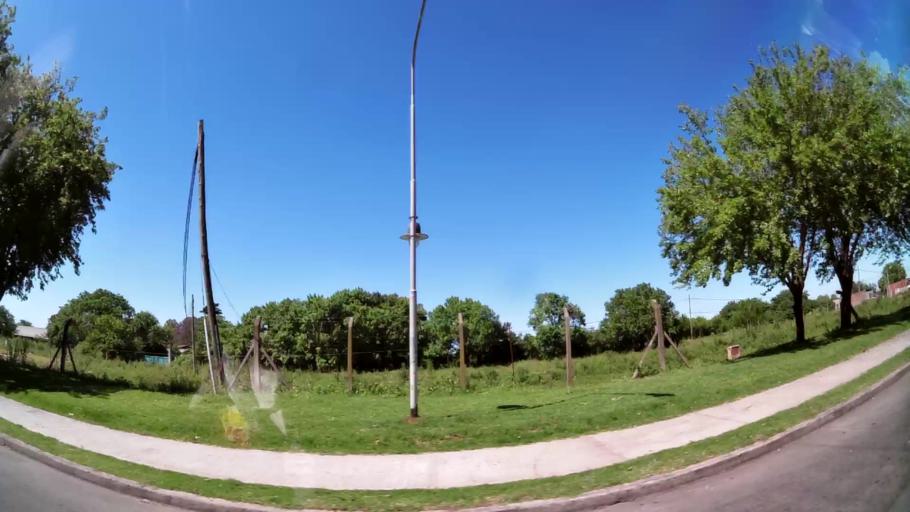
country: AR
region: Buenos Aires
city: Hurlingham
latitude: -34.5032
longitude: -58.6309
